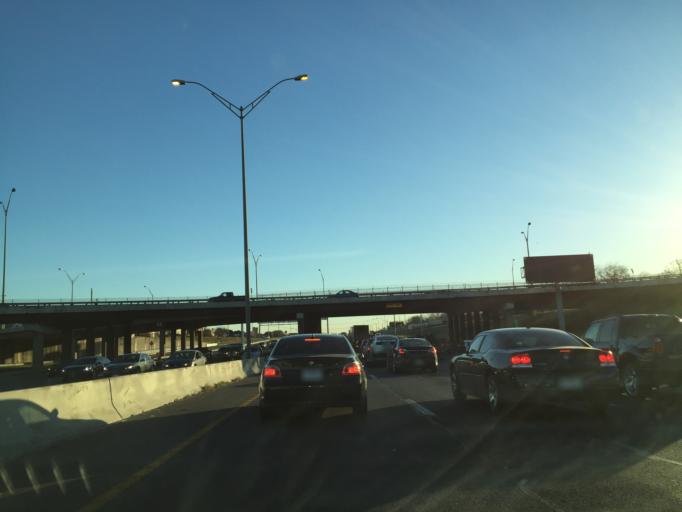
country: US
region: Texas
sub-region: Travis County
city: Austin
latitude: 30.3105
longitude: -97.7098
